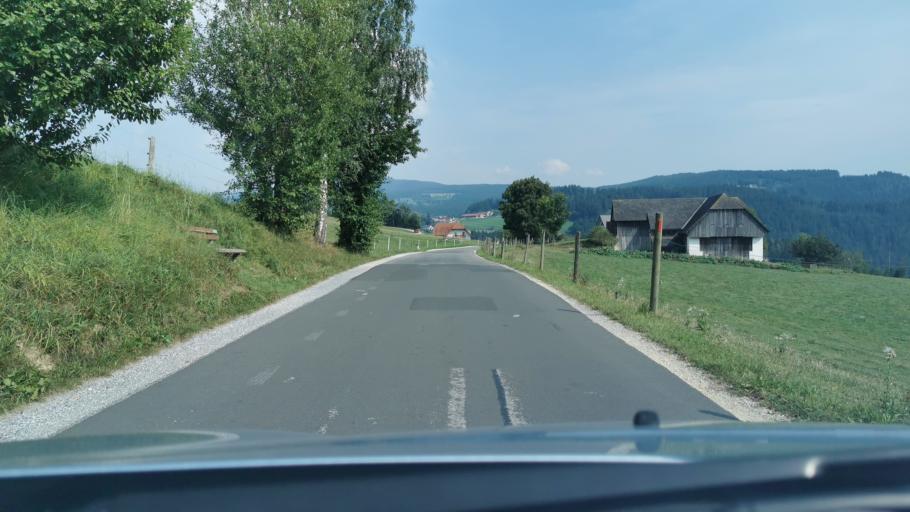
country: AT
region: Styria
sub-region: Politischer Bezirk Weiz
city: Strallegg
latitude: 47.3989
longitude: 15.6908
